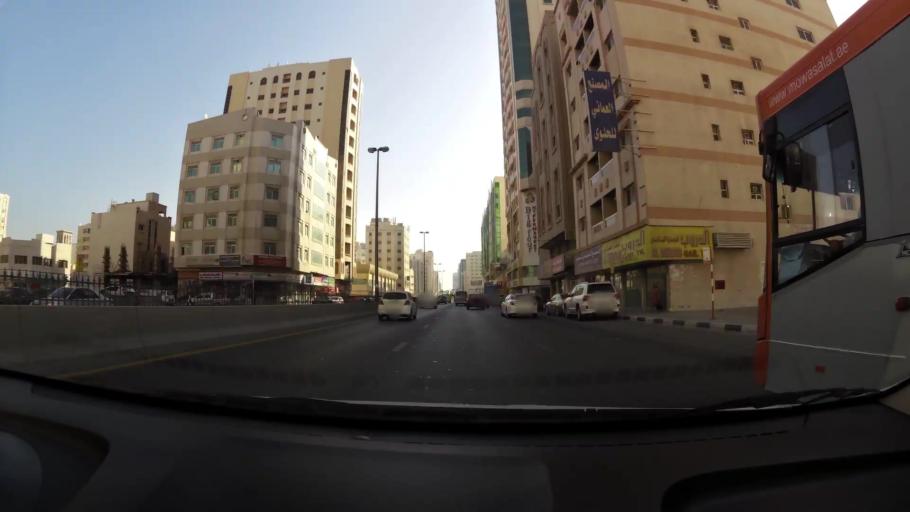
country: AE
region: Ash Shariqah
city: Sharjah
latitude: 25.3665
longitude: 55.3943
